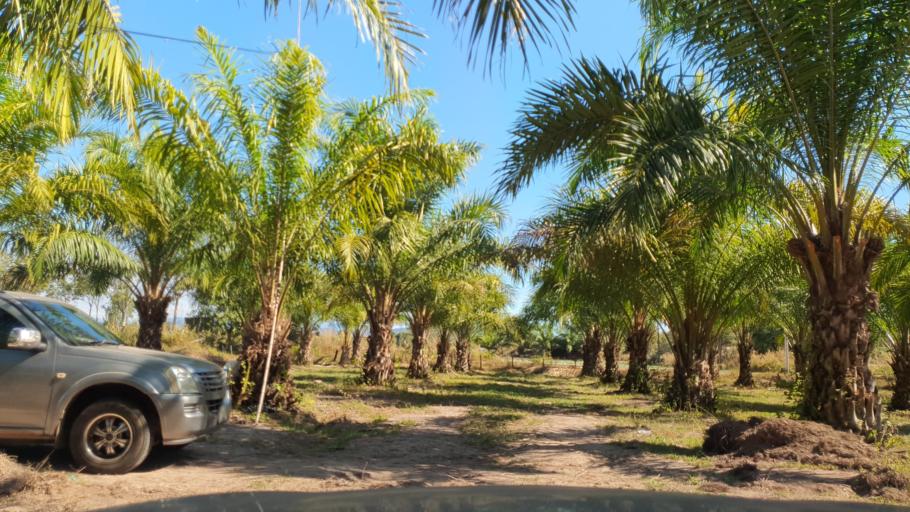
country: TH
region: Nakhon Phanom
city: Ban Phaeng
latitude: 17.9873
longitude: 104.1459
